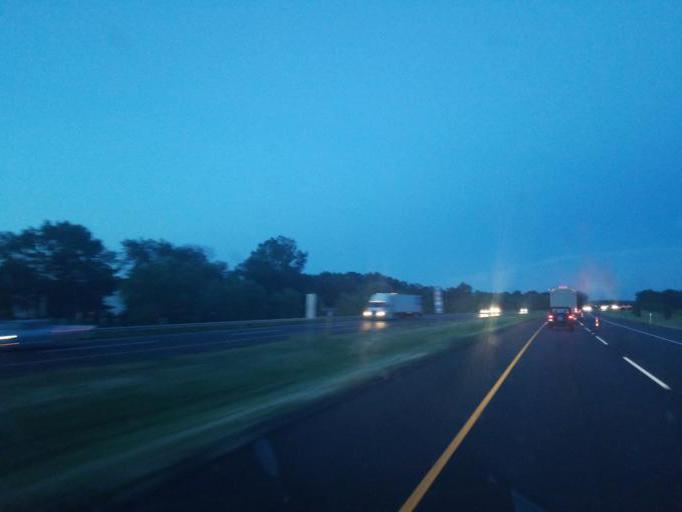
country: US
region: Indiana
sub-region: Saint Joseph County
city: Granger
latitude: 41.7336
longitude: -86.1100
